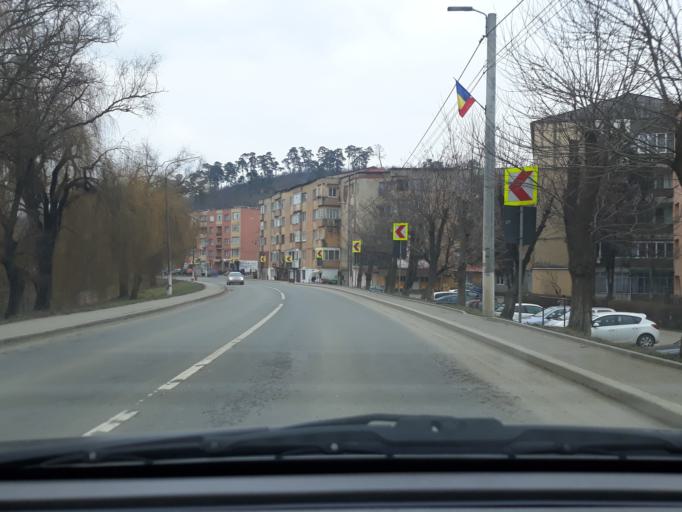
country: RO
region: Salaj
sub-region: Oras Simleu Silvaniei
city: Simleu Silvaniei
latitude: 47.2283
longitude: 22.7895
